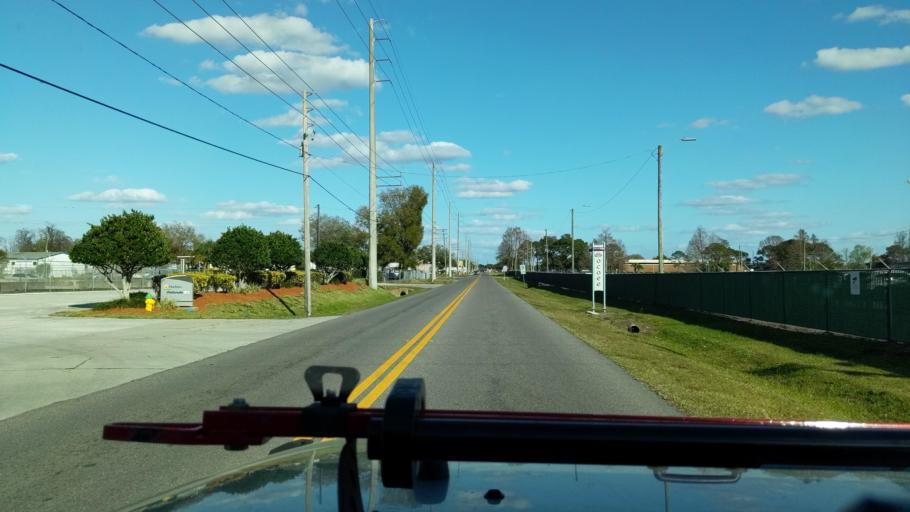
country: US
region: Florida
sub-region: Orange County
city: Ocoee
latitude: 28.5587
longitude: -81.5585
